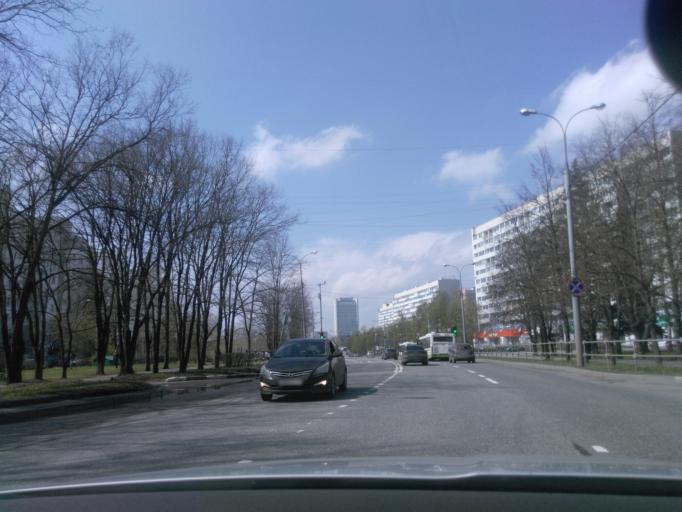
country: RU
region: Moskovskaya
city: Rzhavki
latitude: 55.9872
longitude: 37.2341
